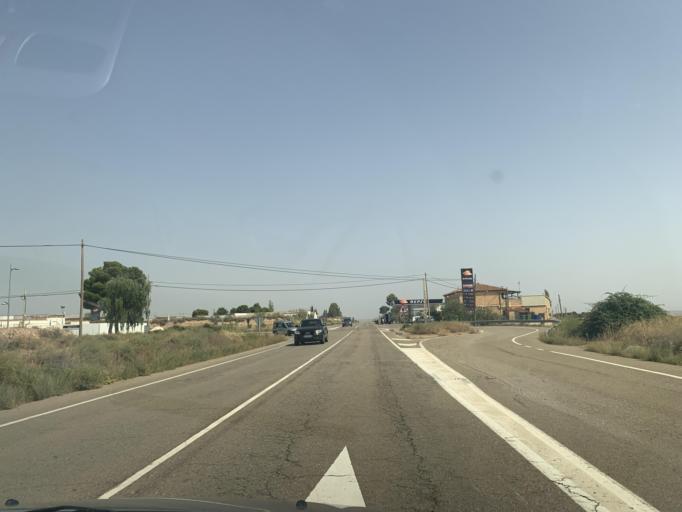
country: ES
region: Aragon
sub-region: Provincia de Zaragoza
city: Belchite
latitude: 41.3084
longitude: -0.7428
